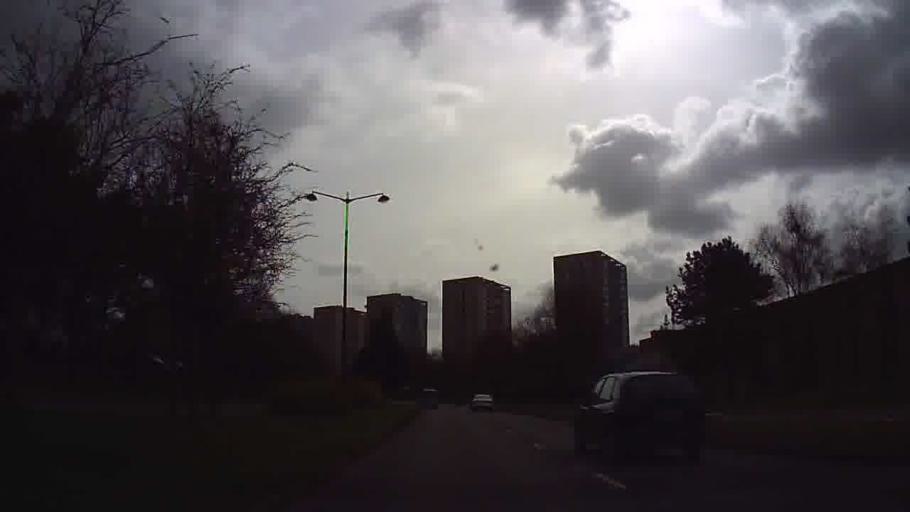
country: FR
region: Brittany
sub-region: Departement d'Ille-et-Vilaine
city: Rennes
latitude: 48.1291
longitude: -1.6662
